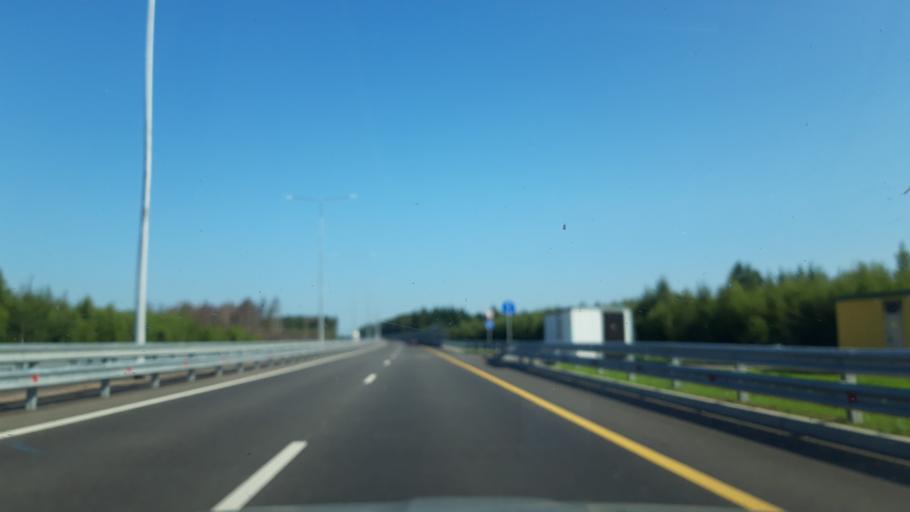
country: RU
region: Moskovskaya
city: Spas-Zaulok
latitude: 56.4789
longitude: 36.5388
